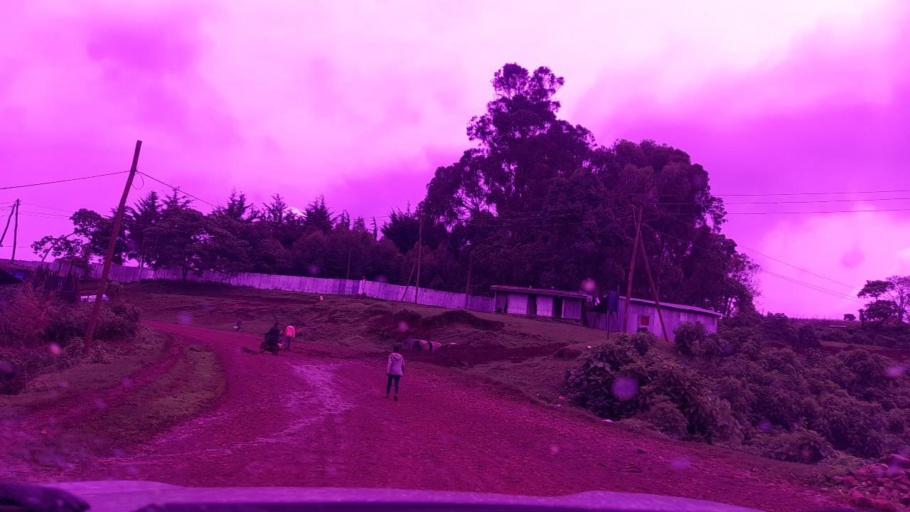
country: ET
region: Southern Nations, Nationalities, and People's Region
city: Tippi
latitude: 7.5947
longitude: 35.7623
